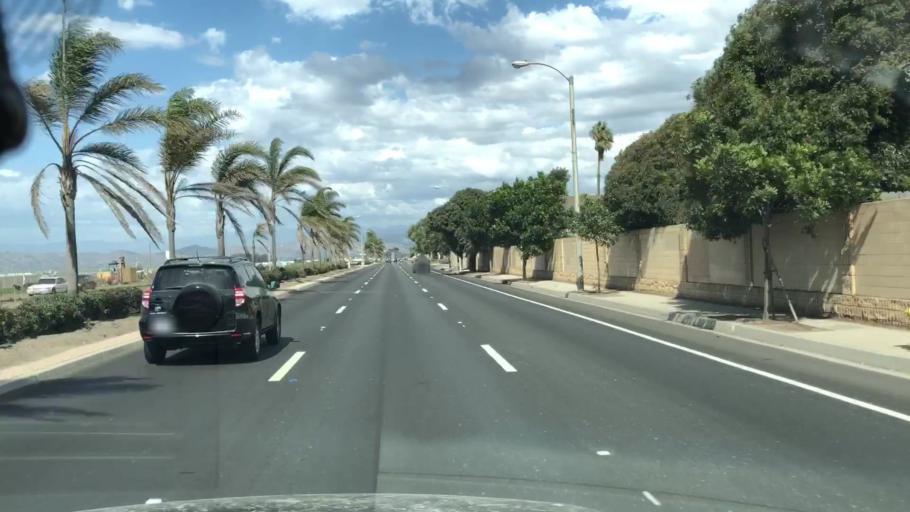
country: US
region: California
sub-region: Ventura County
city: Oxnard Shores
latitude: 34.1929
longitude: -119.2212
